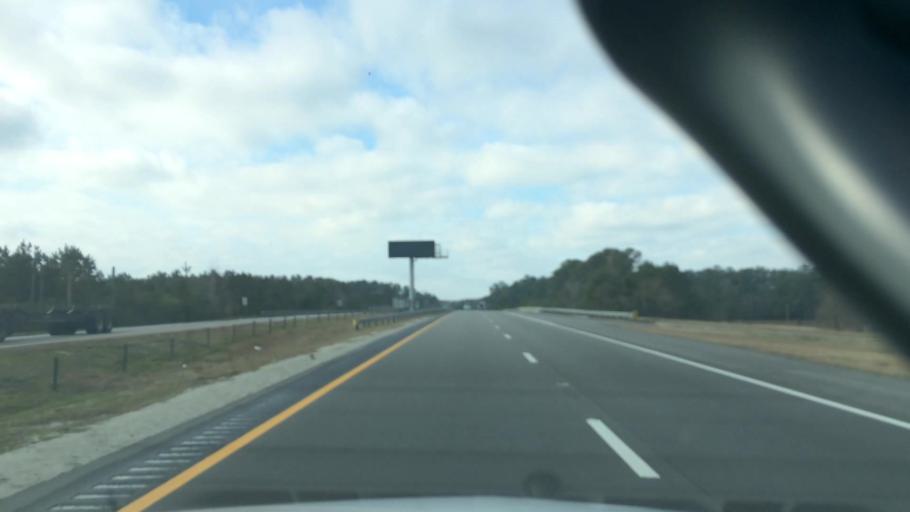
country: US
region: North Carolina
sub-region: New Hanover County
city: Wrightsboro
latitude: 34.3170
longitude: -77.9208
